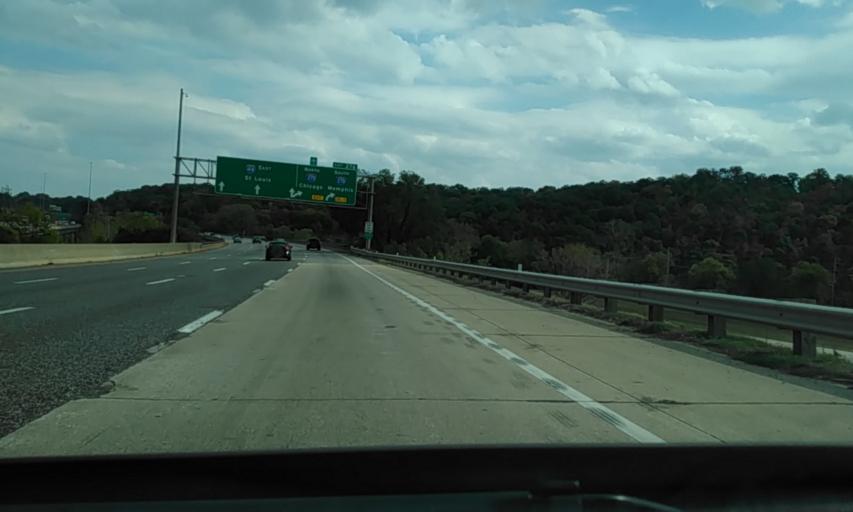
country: US
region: Missouri
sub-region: Saint Louis County
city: Fenton
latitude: 38.5426
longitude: -90.4376
